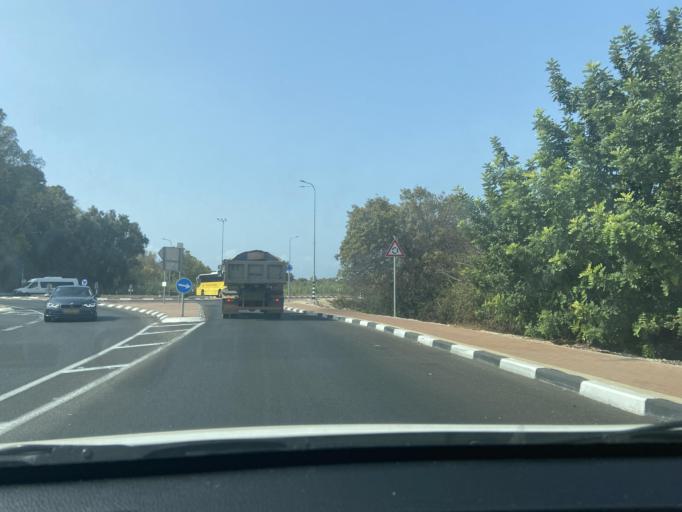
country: IL
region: Northern District
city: Nahariya
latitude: 33.0454
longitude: 35.1065
